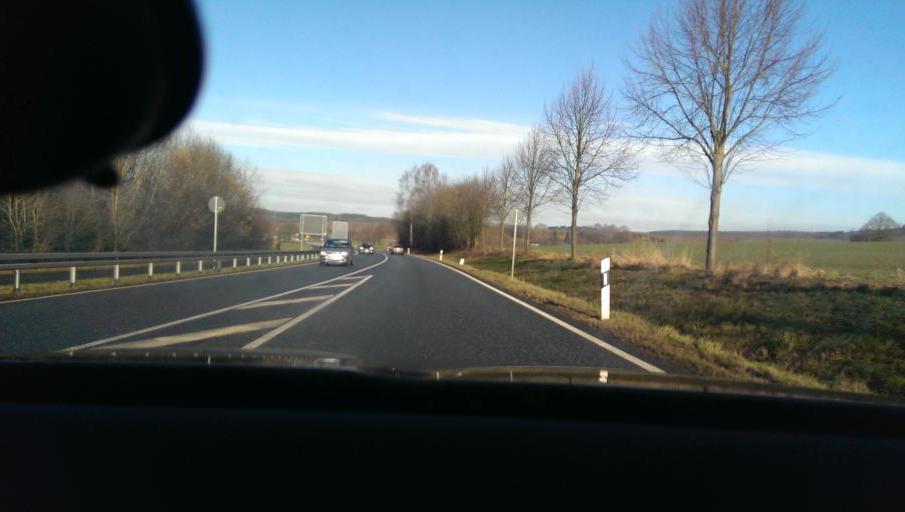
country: DE
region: Hesse
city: Hain-Grundau
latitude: 50.2326
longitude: 9.1379
